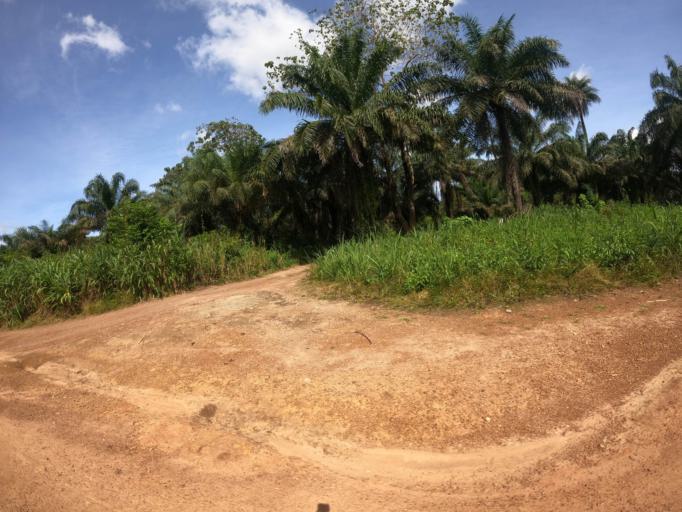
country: SL
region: Northern Province
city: Makeni
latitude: 8.8475
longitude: -12.0301
